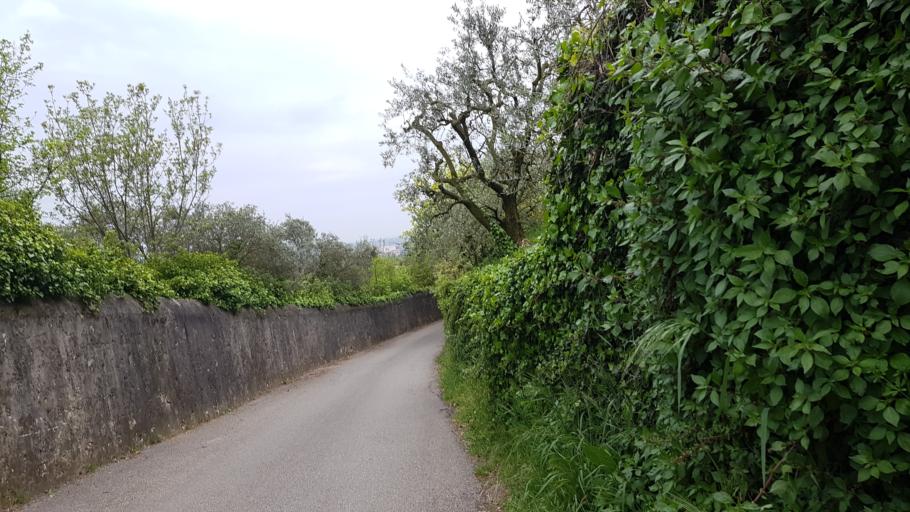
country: IT
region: Veneto
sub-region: Provincia di Verona
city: Parona
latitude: 45.4756
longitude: 10.9714
